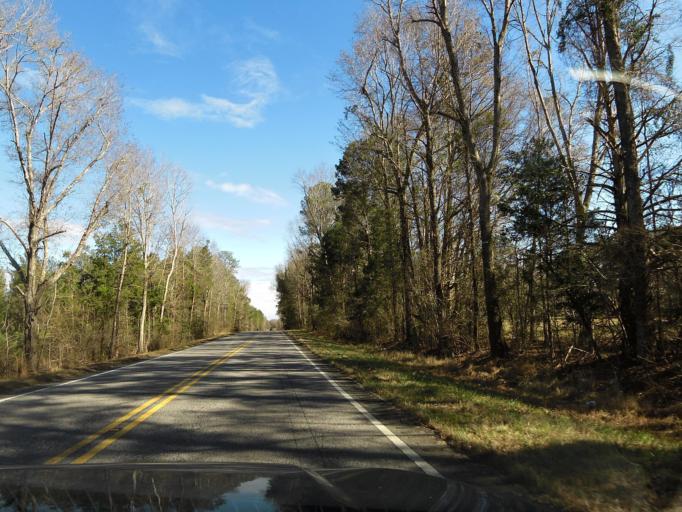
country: US
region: Alabama
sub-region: Barbour County
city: Clayton
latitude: 32.0345
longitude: -85.3923
